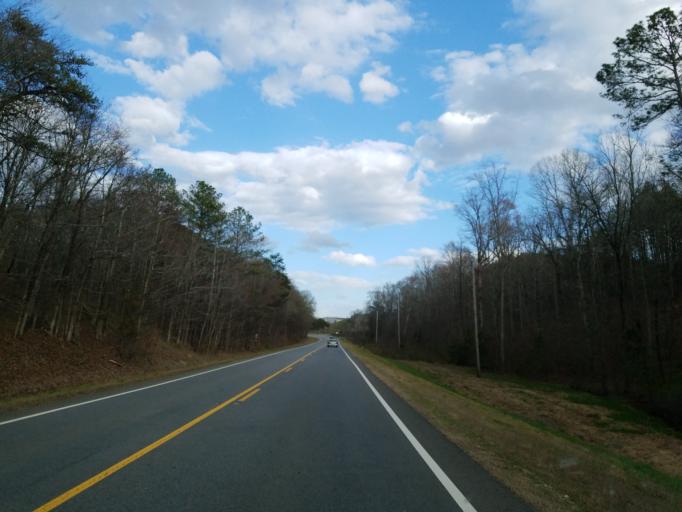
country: US
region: Georgia
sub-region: Bartow County
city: Rydal
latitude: 34.4466
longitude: -84.7510
